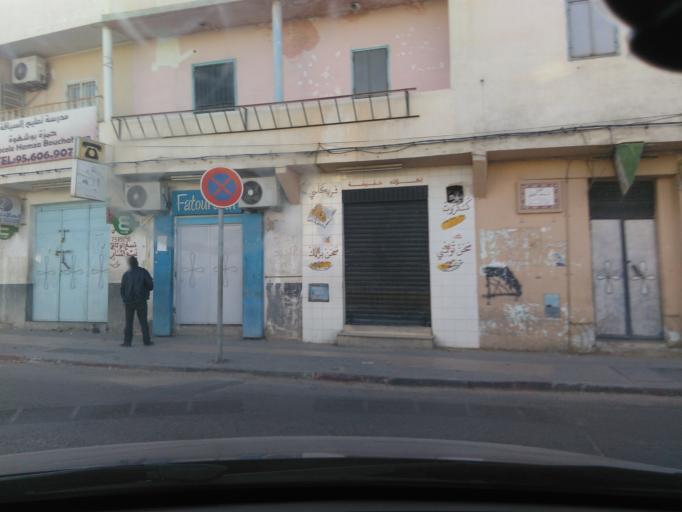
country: TN
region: Tataouine
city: Tataouine
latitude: 32.9316
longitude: 10.4504
